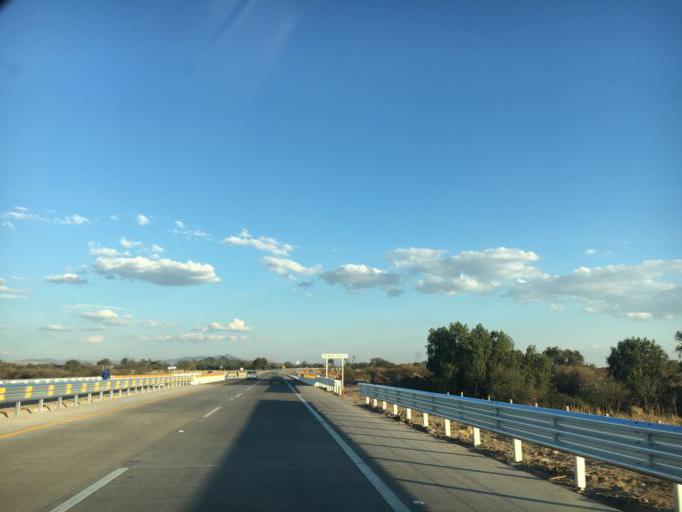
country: MX
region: Guanajuato
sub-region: Leon
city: Fraccionamiento Paraiso Real
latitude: 21.0977
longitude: -101.5702
